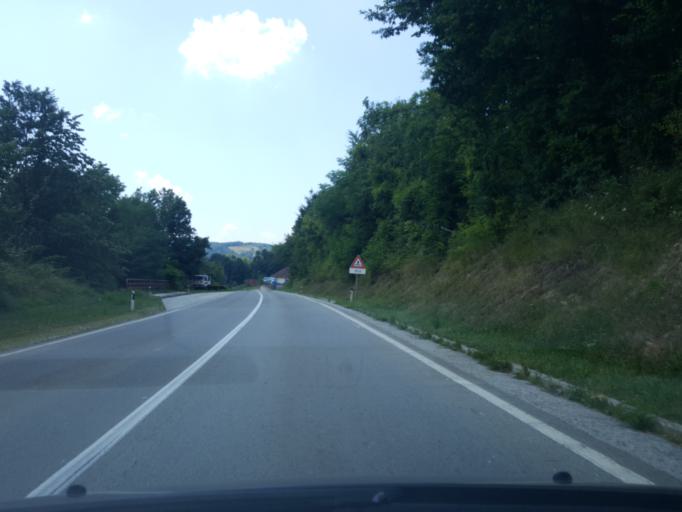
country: RS
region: Central Serbia
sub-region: Moravicki Okrug
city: Gornji Milanovac
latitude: 44.1030
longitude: 20.4819
